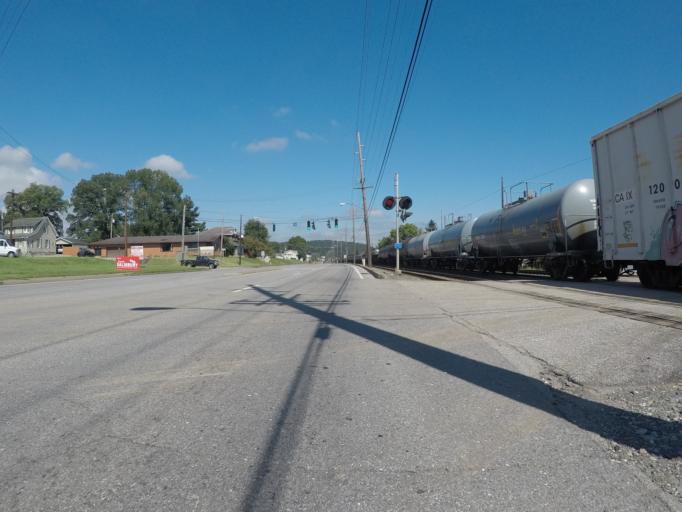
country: US
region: Ohio
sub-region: Lawrence County
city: South Point
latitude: 38.4422
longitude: -82.6097
